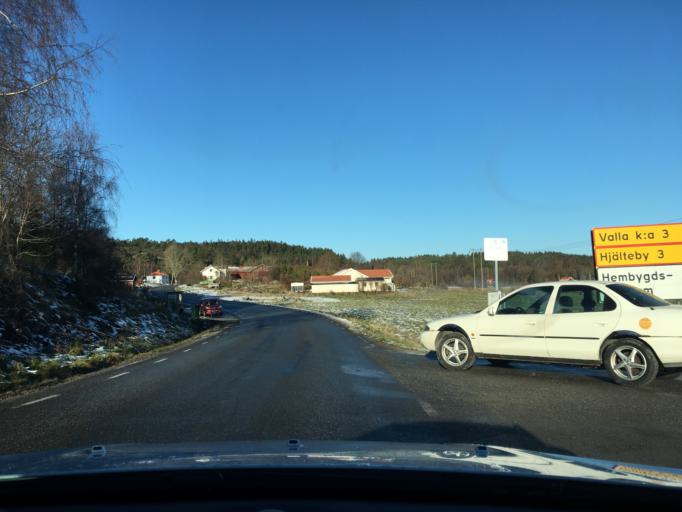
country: SE
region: Vaestra Goetaland
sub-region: Tjorns Kommun
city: Myggenas
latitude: 58.0395
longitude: 11.6744
